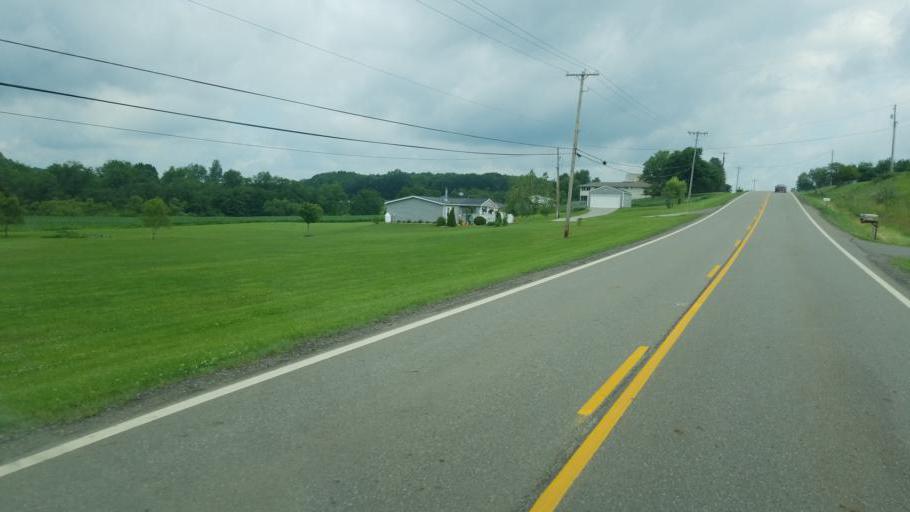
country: US
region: Ohio
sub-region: Columbiana County
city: Lisbon
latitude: 40.7279
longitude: -80.7899
